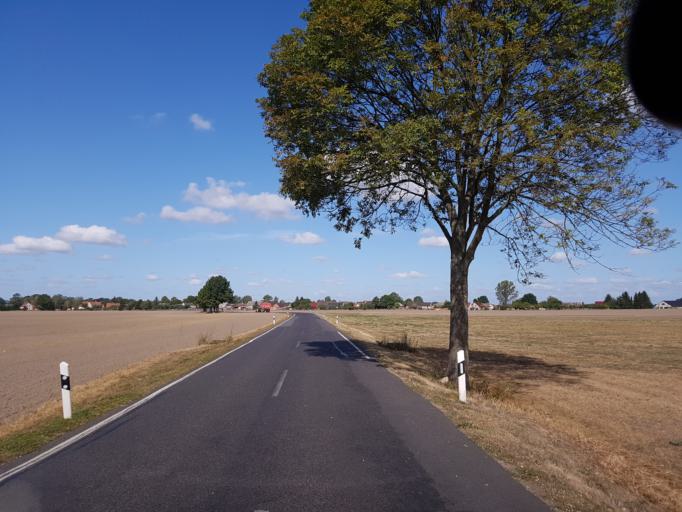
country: DE
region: Brandenburg
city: Sonnewalde
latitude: 51.7072
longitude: 13.6424
